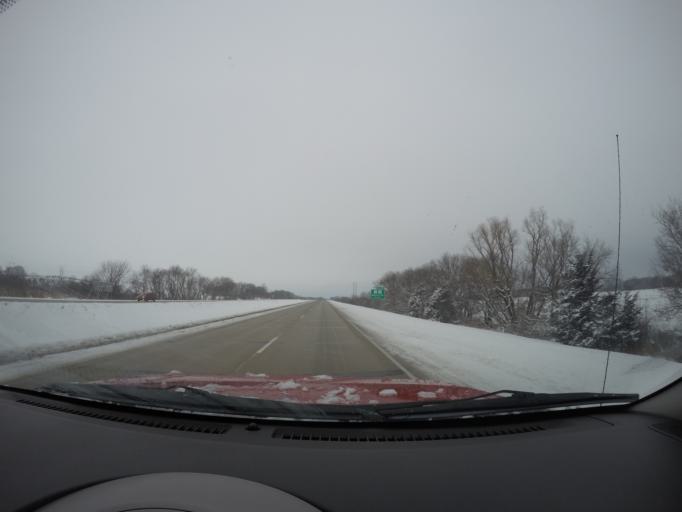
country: US
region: Minnesota
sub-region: Olmsted County
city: Rochester
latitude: 43.9543
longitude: -92.3656
